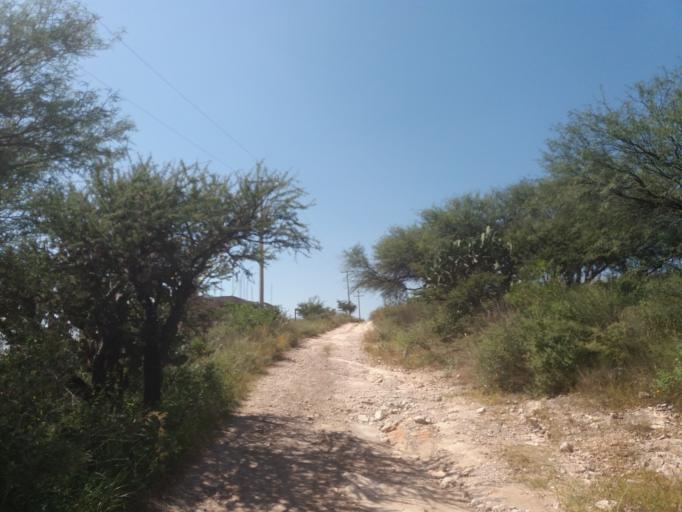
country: MX
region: Aguascalientes
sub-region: Aguascalientes
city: San Sebastian [Fraccionamiento]
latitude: 21.7730
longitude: -102.2342
